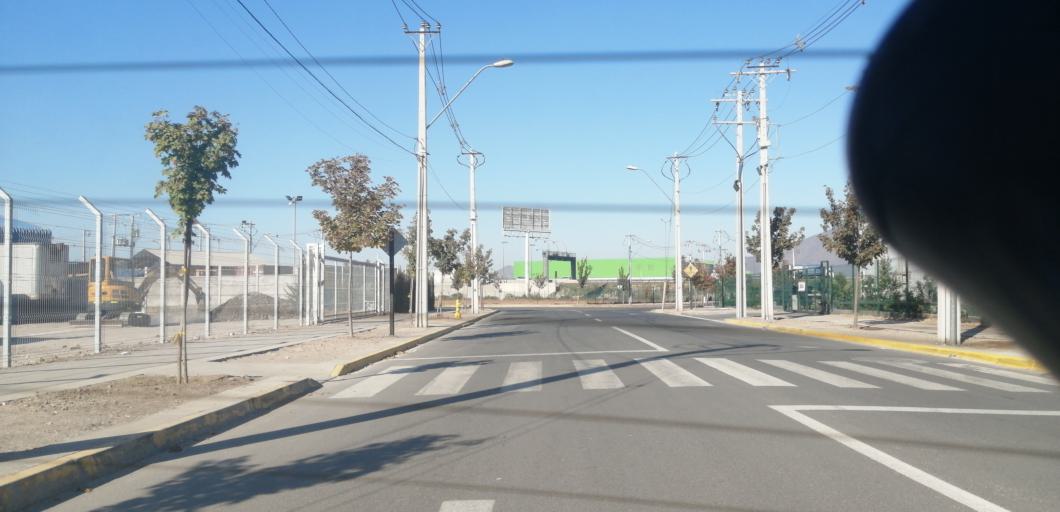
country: CL
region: Santiago Metropolitan
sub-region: Provincia de Santiago
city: Lo Prado
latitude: -33.4371
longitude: -70.7819
